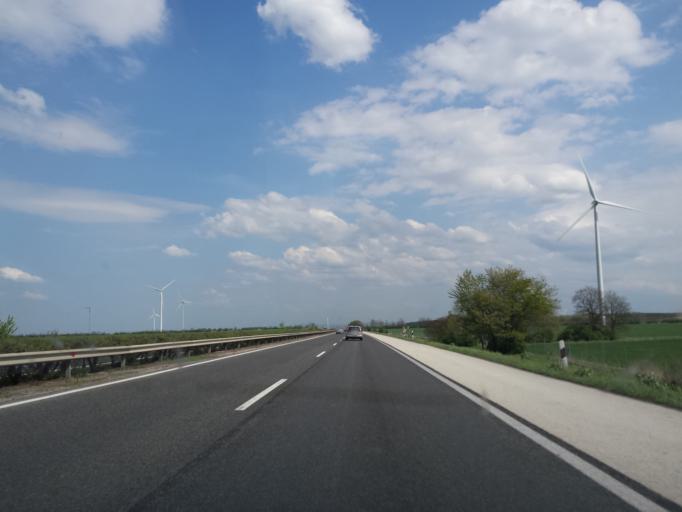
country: HU
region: Komarom-Esztergom
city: Babolna
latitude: 47.6794
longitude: 17.9260
